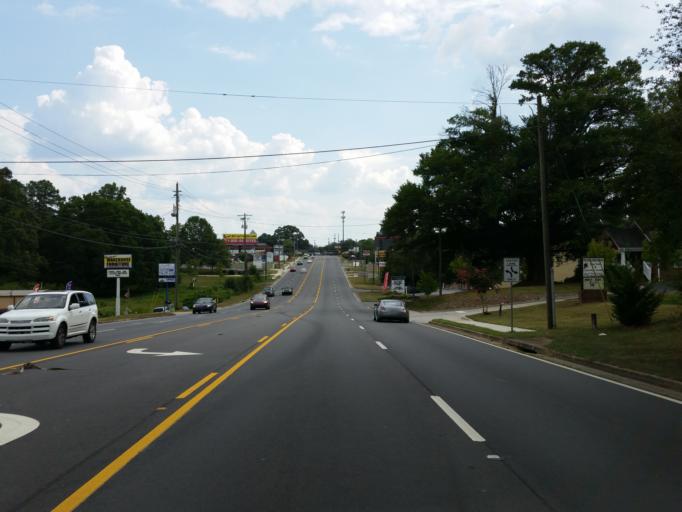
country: US
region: Georgia
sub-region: Cobb County
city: Marietta
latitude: 34.0144
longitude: -84.5274
